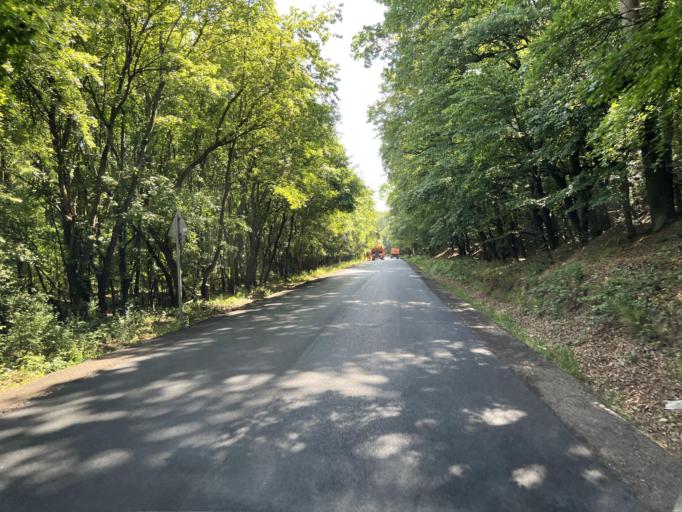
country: HU
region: Pest
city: Valko
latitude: 47.5686
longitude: 19.4696
